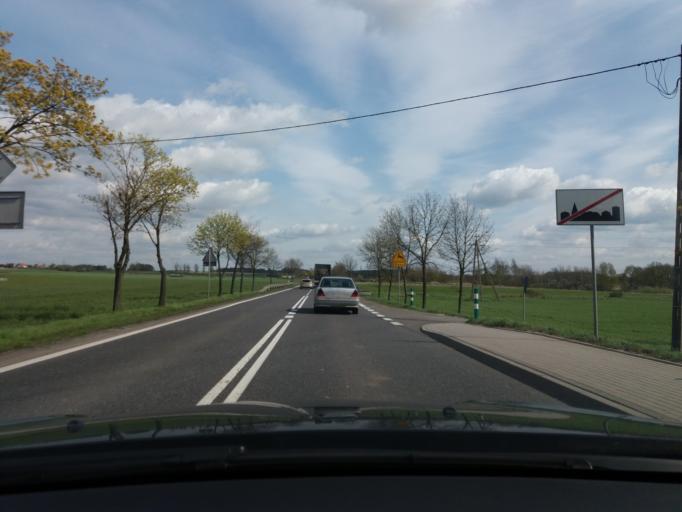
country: PL
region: Lower Silesian Voivodeship
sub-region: Powiat sredzki
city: Malczyce
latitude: 51.1988
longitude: 16.4848
